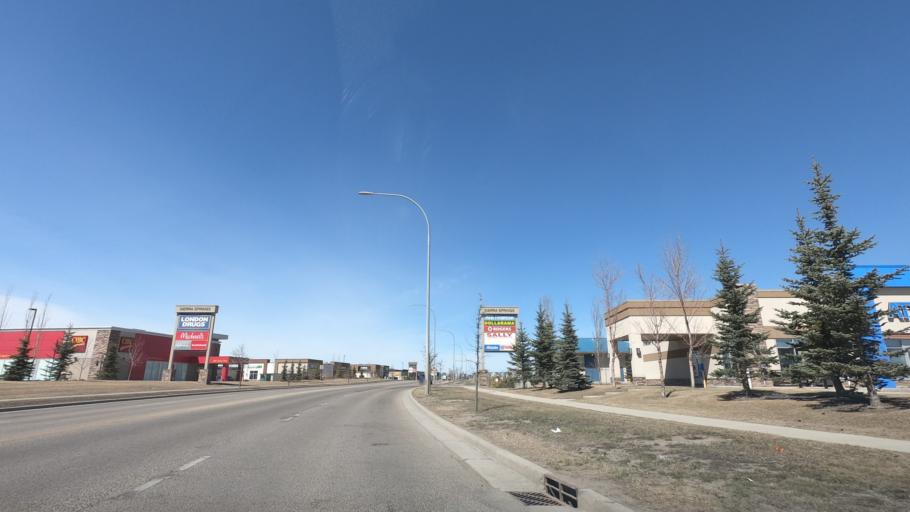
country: CA
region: Alberta
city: Airdrie
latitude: 51.2649
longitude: -114.0059
